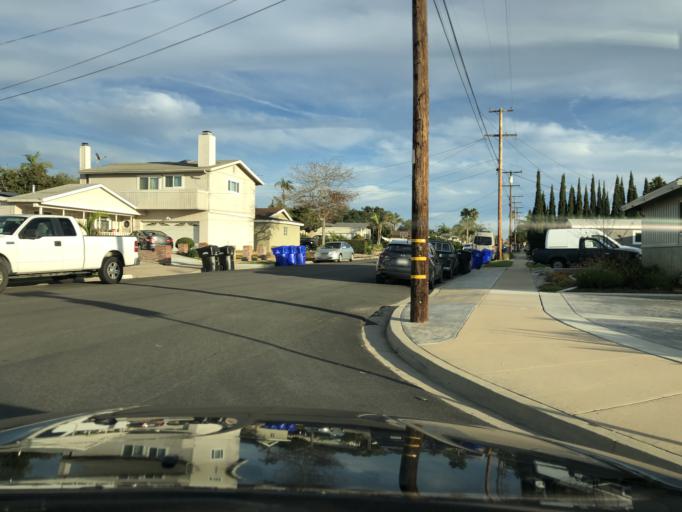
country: US
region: California
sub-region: San Diego County
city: La Jolla
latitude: 32.8269
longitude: -117.1903
